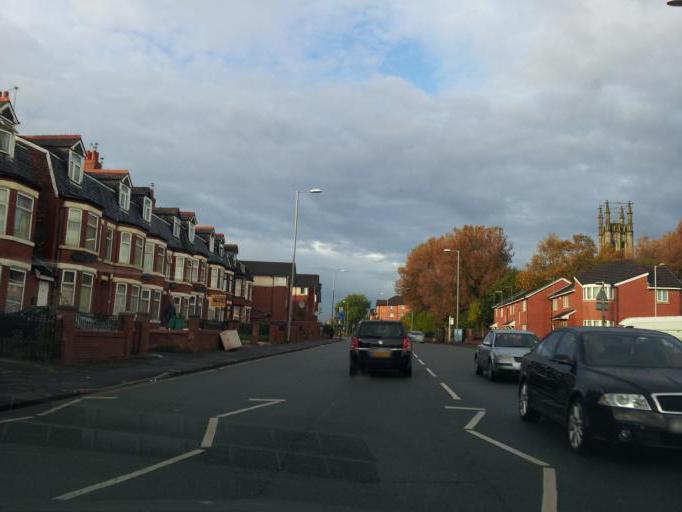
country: GB
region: England
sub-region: Manchester
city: Cheetham Hill
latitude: 53.5027
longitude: -2.2358
